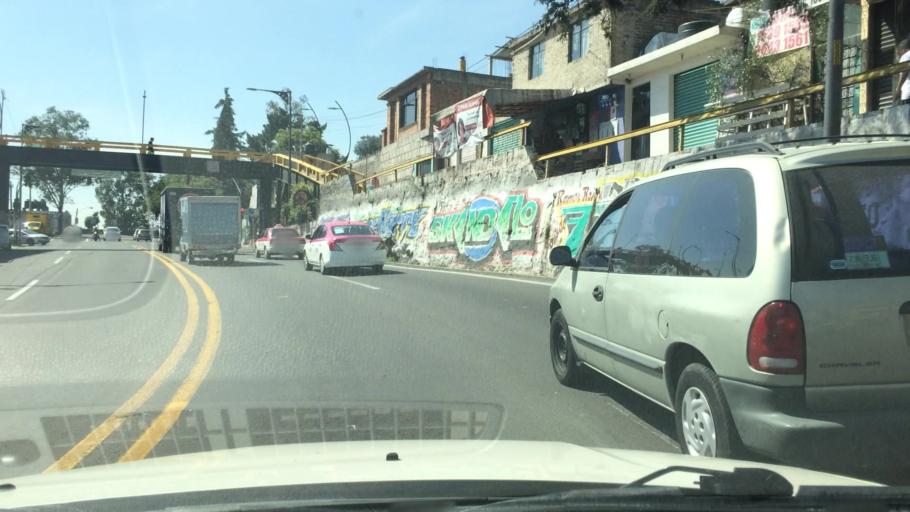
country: MX
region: Mexico City
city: Tlalpan
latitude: 19.2545
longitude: -99.1776
